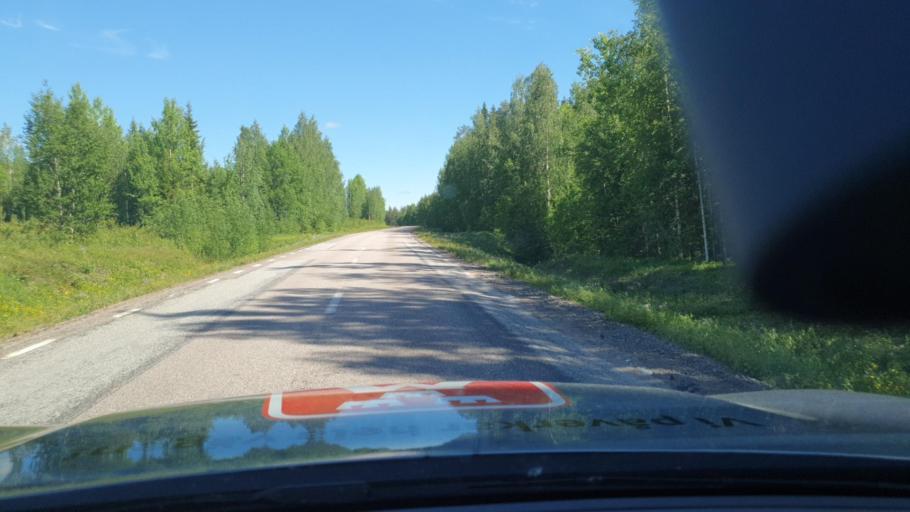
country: SE
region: Norrbotten
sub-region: Overkalix Kommun
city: OEverkalix
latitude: 66.8071
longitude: 22.7368
